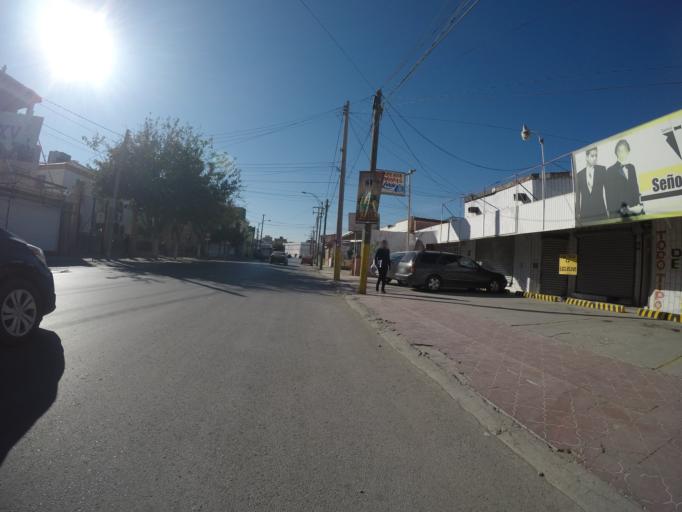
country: MX
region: Chihuahua
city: Ciudad Juarez
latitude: 31.7425
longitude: -106.4815
